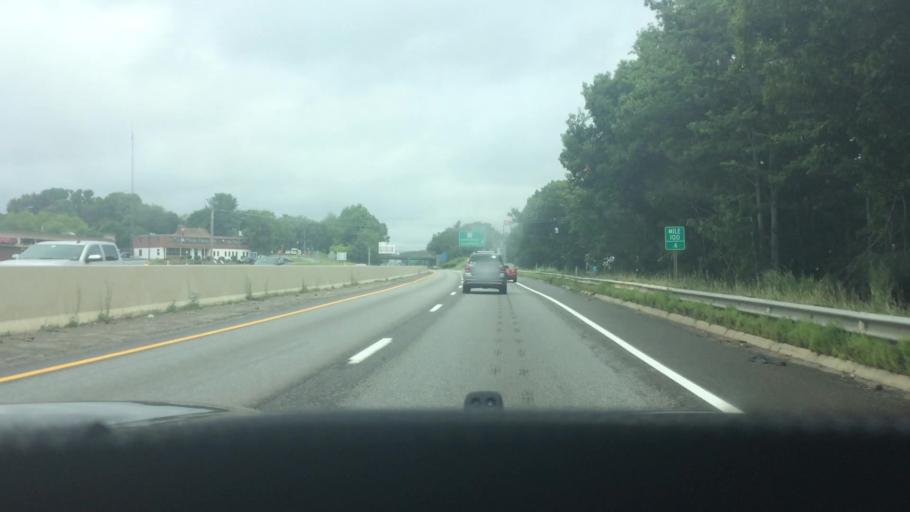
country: US
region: Massachusetts
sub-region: Worcester County
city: Leominster
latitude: 42.5348
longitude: -71.7402
